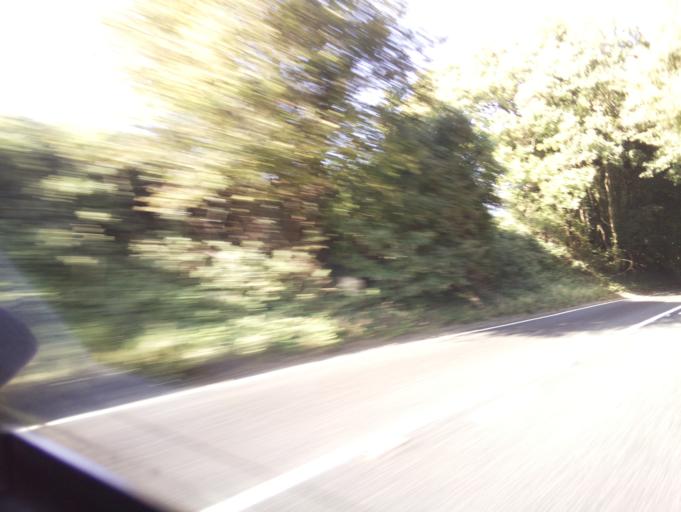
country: GB
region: England
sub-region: Hampshire
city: Four Marks
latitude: 51.0207
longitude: -1.0802
